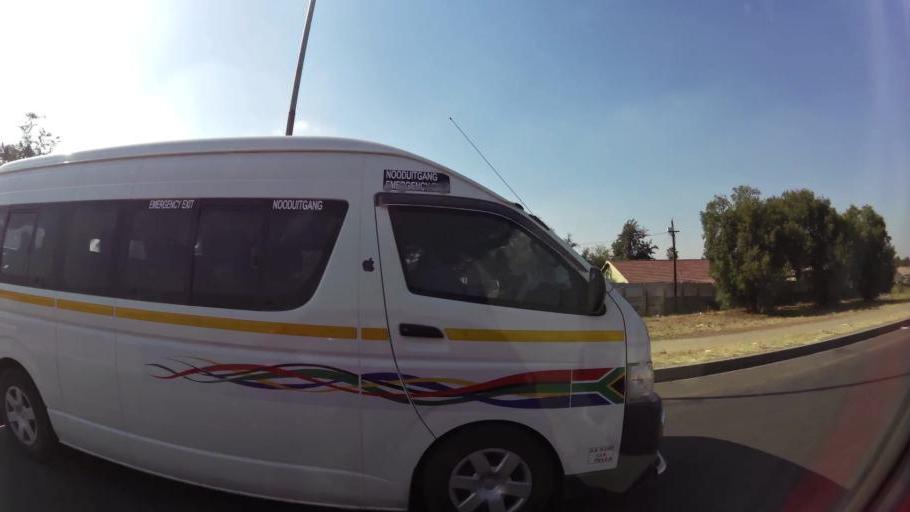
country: ZA
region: North-West
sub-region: Bojanala Platinum District Municipality
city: Rustenburg
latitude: -25.6567
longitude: 27.2237
